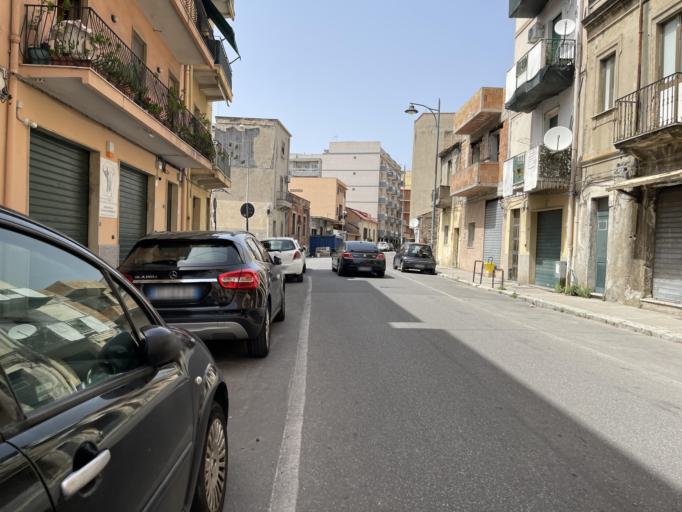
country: IT
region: Calabria
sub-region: Provincia di Reggio Calabria
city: Reggio Calabria
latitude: 38.0952
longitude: 15.6435
